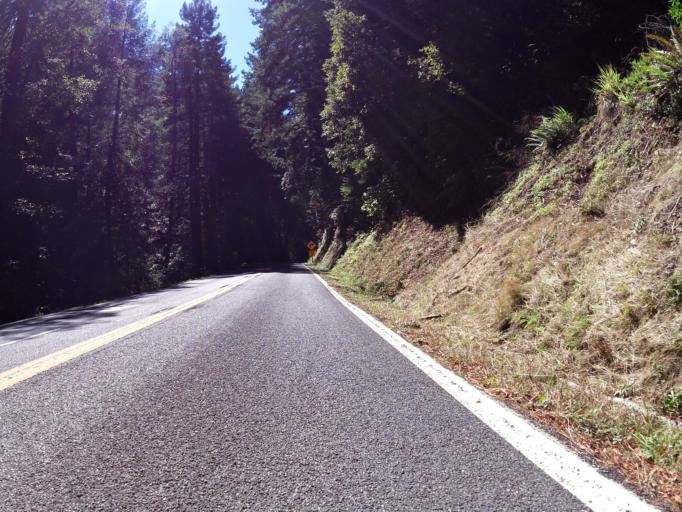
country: US
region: California
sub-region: Humboldt County
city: Redway
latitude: 39.7884
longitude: -123.8174
